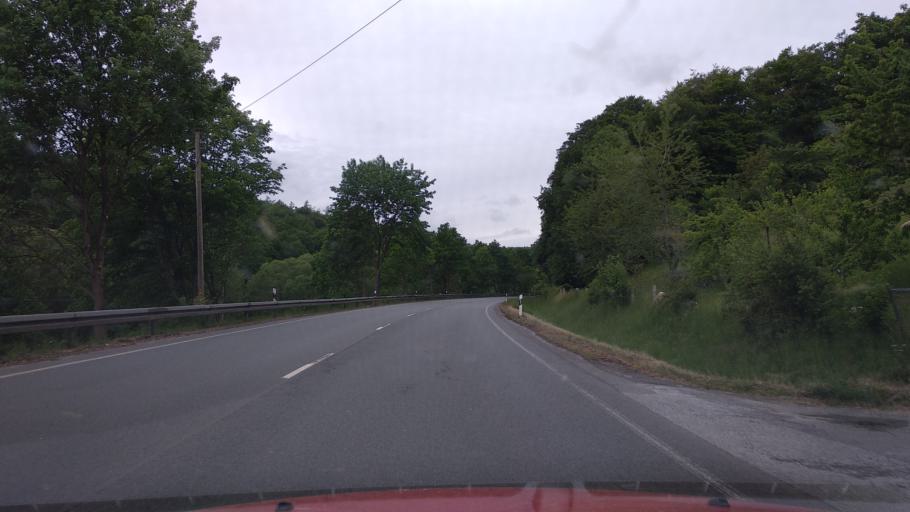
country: DE
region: North Rhine-Westphalia
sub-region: Regierungsbezirk Detmold
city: Willebadessen
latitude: 51.6240
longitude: 9.0927
